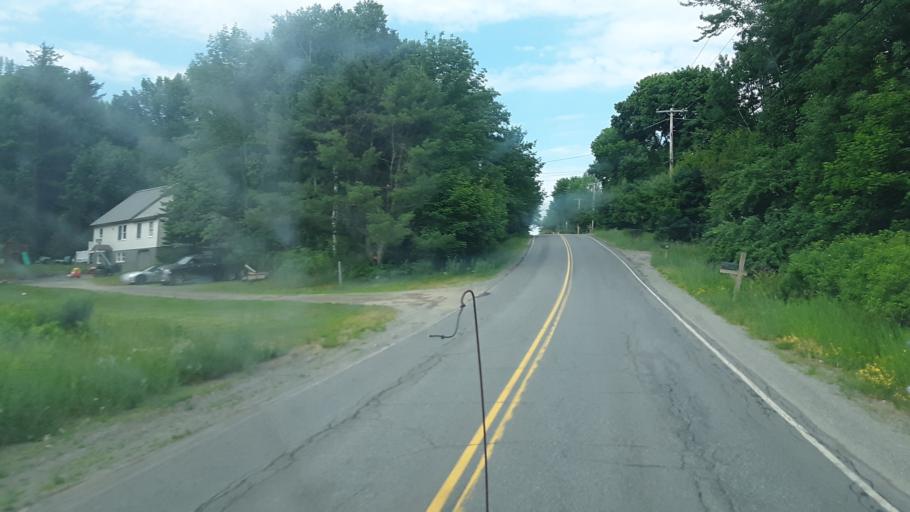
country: US
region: Maine
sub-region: Penobscot County
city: Hampden
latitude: 44.7293
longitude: -68.8708
